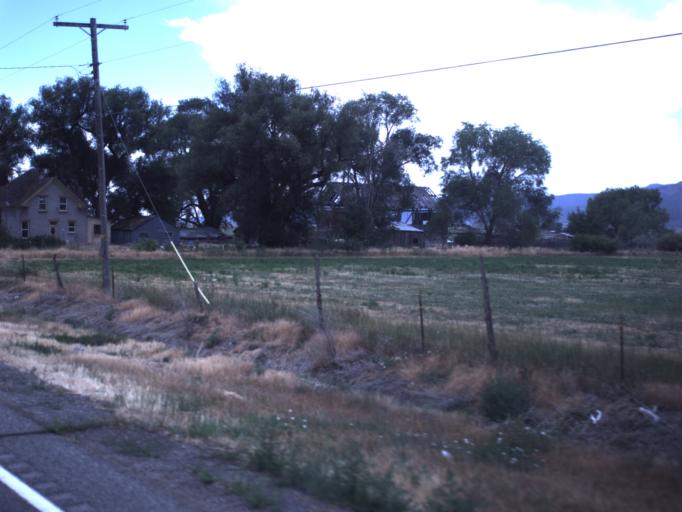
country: US
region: Utah
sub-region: Sanpete County
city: Moroni
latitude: 39.4731
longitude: -111.5629
